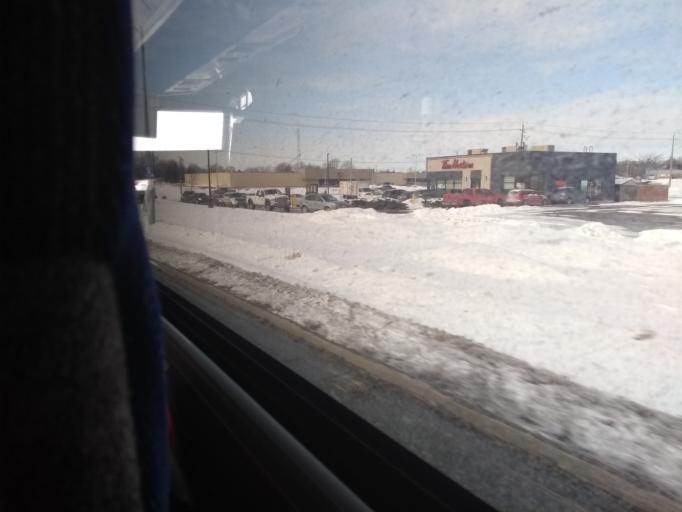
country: CA
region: Ontario
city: Welland
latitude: 42.9936
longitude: -79.2247
